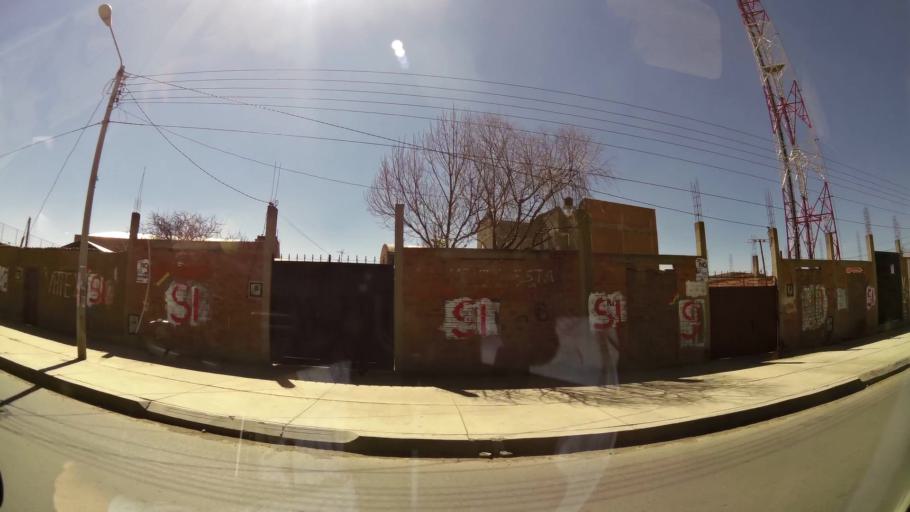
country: BO
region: La Paz
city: La Paz
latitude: -16.5230
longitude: -68.2192
